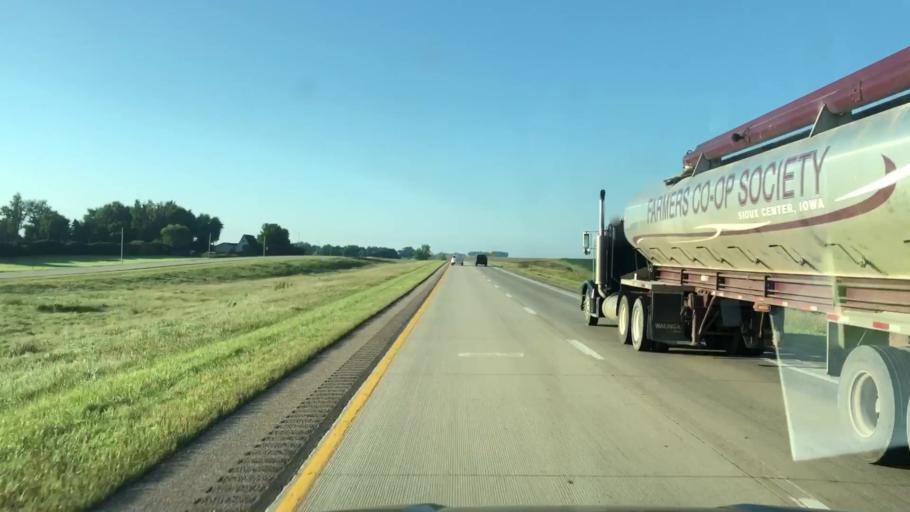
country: US
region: Iowa
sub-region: Sioux County
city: Alton
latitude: 43.0437
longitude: -95.9203
